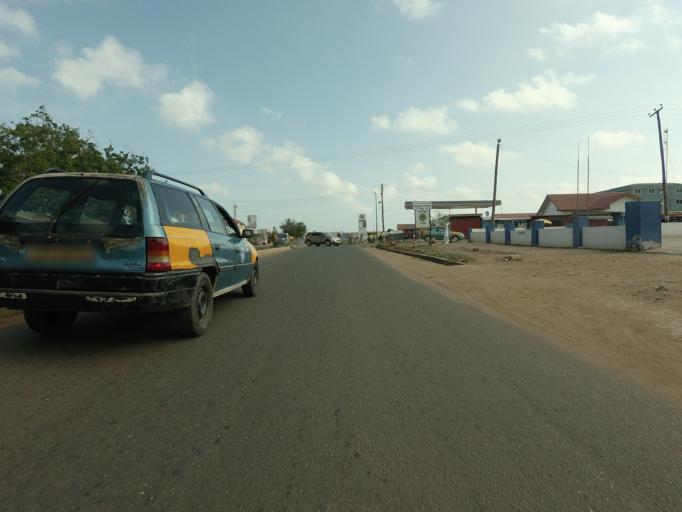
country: GH
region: Greater Accra
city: Tema
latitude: 5.6605
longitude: -0.0515
